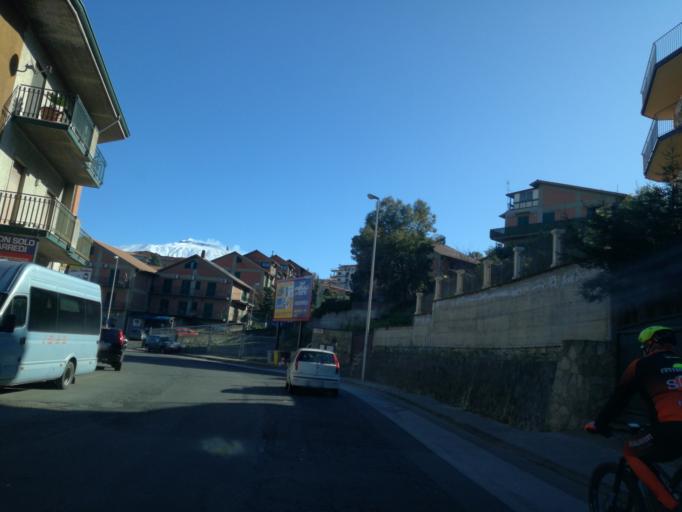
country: IT
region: Sicily
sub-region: Catania
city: Bronte
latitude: 37.7818
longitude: 14.8340
